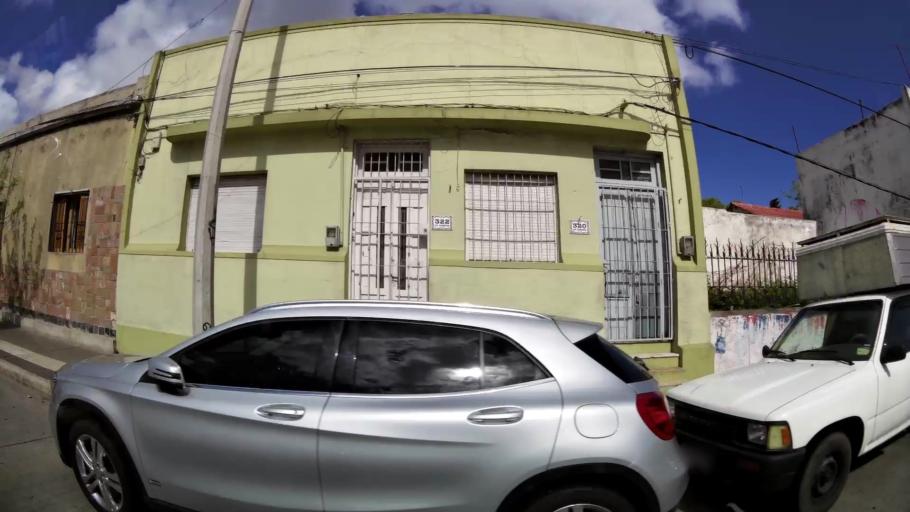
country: UY
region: Montevideo
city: Montevideo
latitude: -34.8480
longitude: -56.2230
